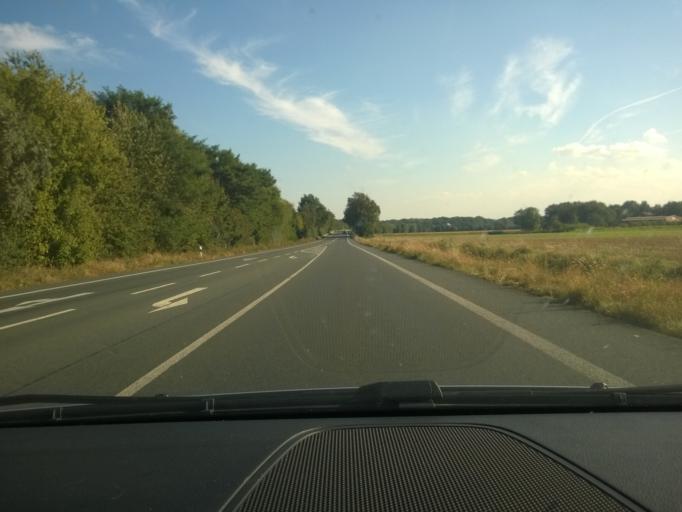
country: DE
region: North Rhine-Westphalia
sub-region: Regierungsbezirk Munster
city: Sudlohn
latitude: 51.9045
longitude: 6.8515
